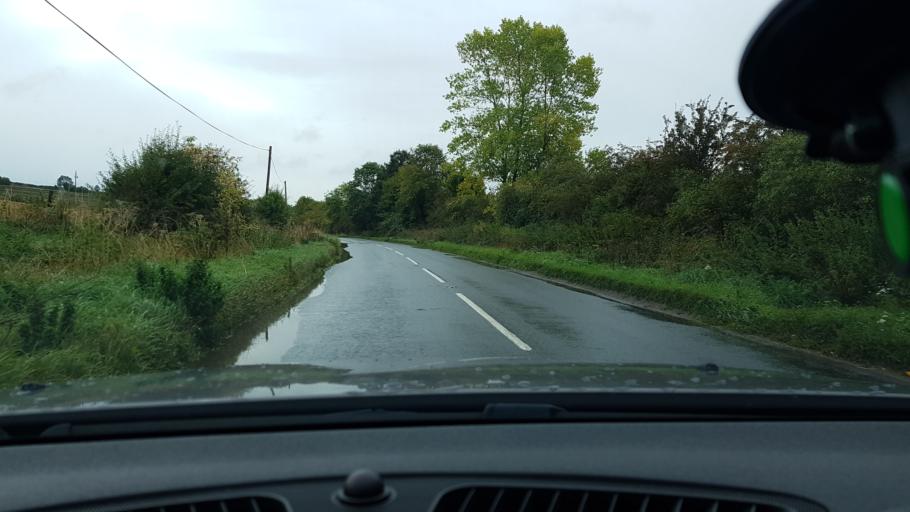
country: GB
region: England
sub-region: West Berkshire
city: Lambourn
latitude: 51.5192
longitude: -1.5230
